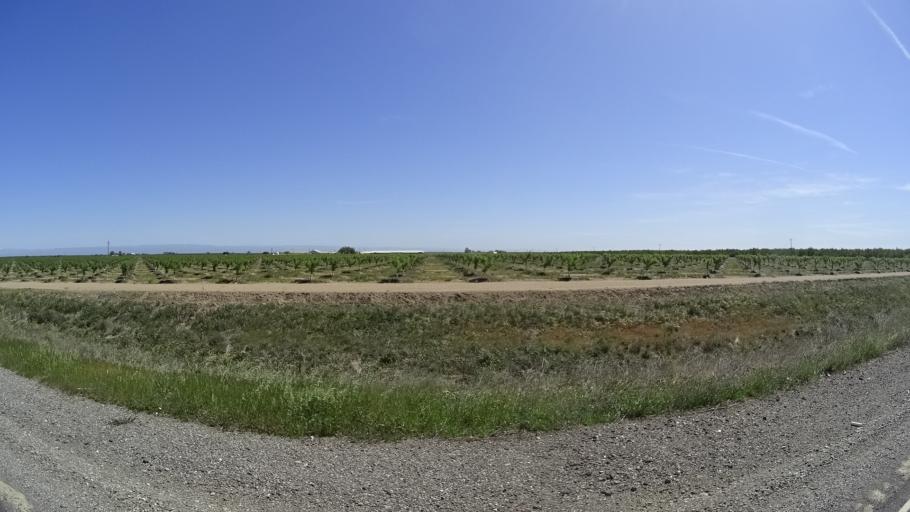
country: US
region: California
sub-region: Glenn County
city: Orland
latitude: 39.6399
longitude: -122.1410
